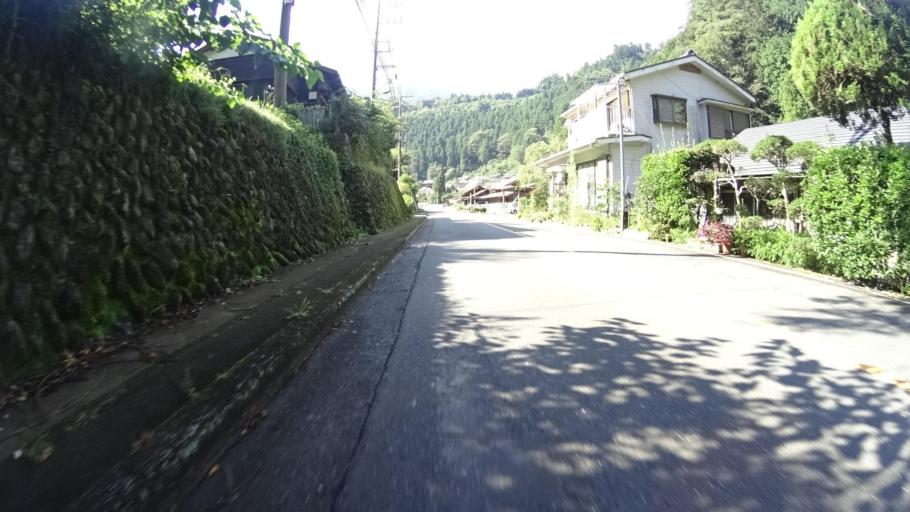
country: JP
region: Tokyo
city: Itsukaichi
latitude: 35.7402
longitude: 139.1223
